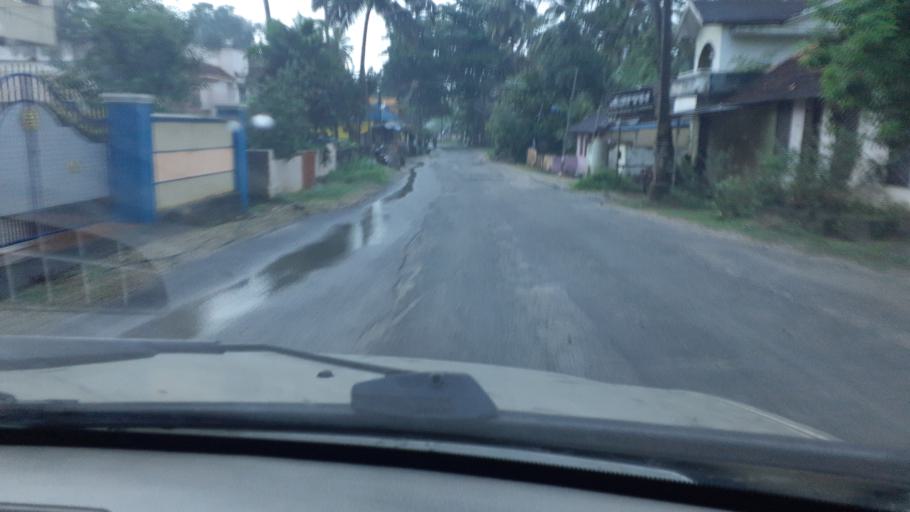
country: IN
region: Tamil Nadu
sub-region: Kanniyakumari
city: Padmanabhapuram
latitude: 8.3630
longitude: 77.3114
